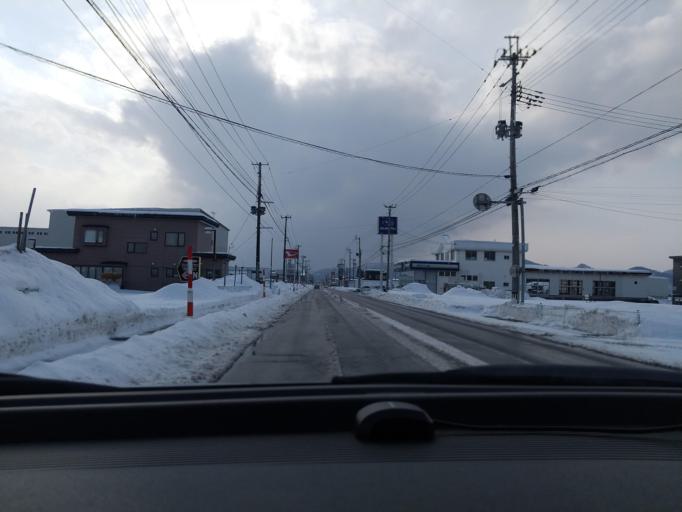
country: JP
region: Akita
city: Omagari
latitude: 39.4830
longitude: 140.4873
